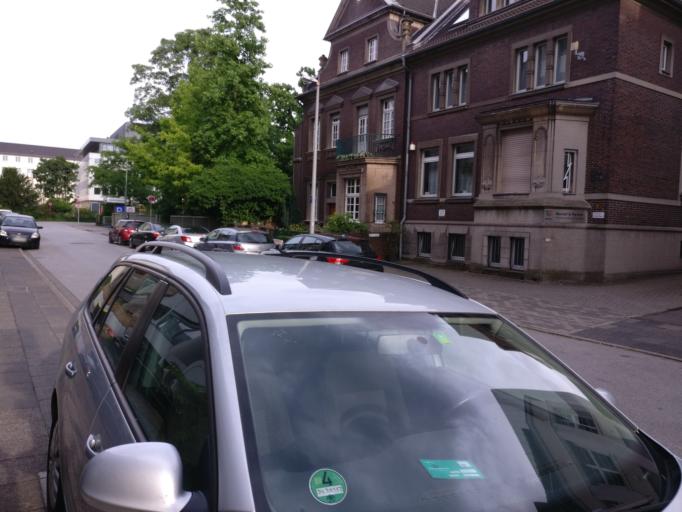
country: DE
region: North Rhine-Westphalia
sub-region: Regierungsbezirk Dusseldorf
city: Duisburg
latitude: 51.4343
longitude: 6.7667
